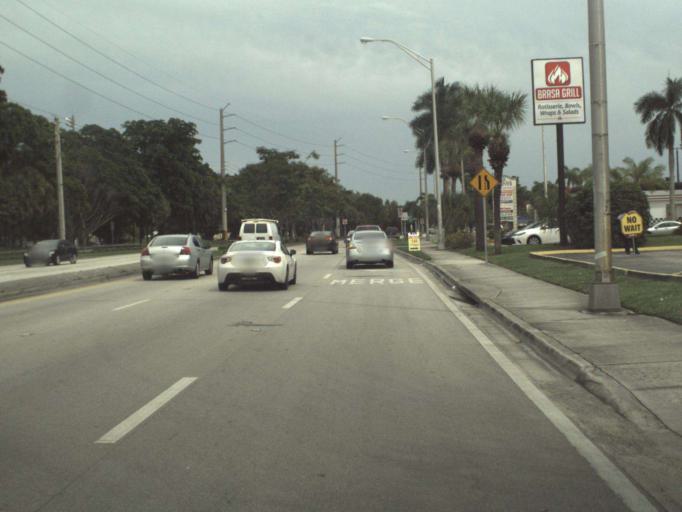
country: US
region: Florida
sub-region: Miami-Dade County
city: Country Club
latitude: 25.9423
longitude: -80.3064
